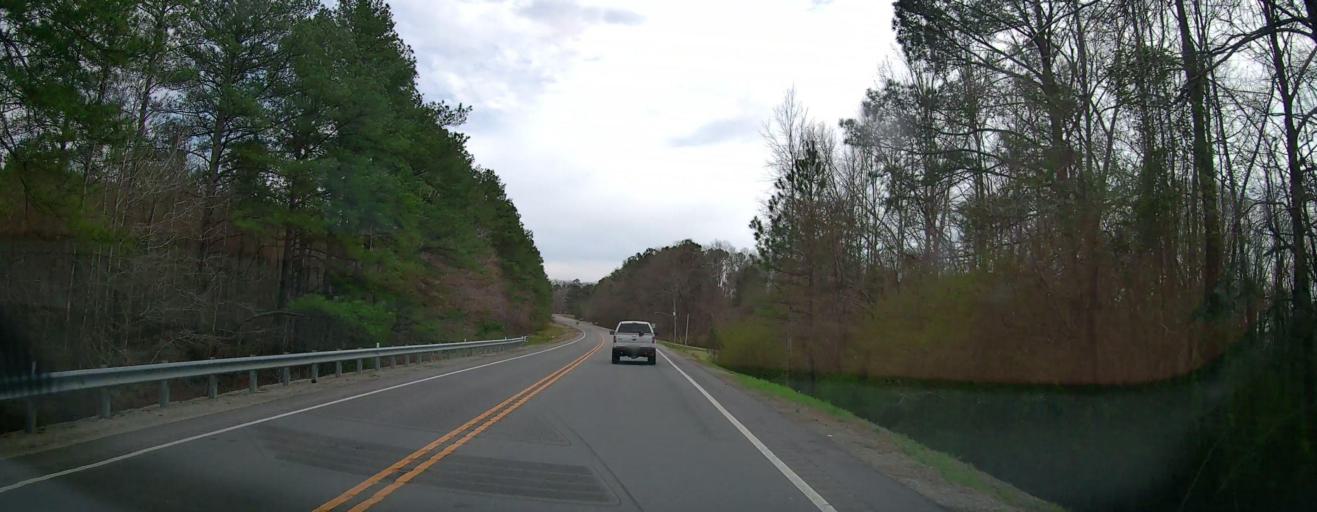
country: US
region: Alabama
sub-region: Marion County
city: Guin
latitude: 33.9943
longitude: -87.9287
